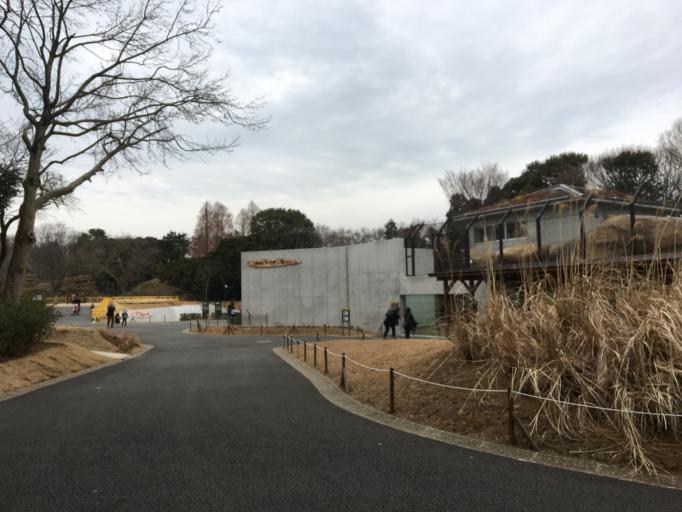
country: JP
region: Chiba
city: Yotsukaido
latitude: 35.6464
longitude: 140.1269
